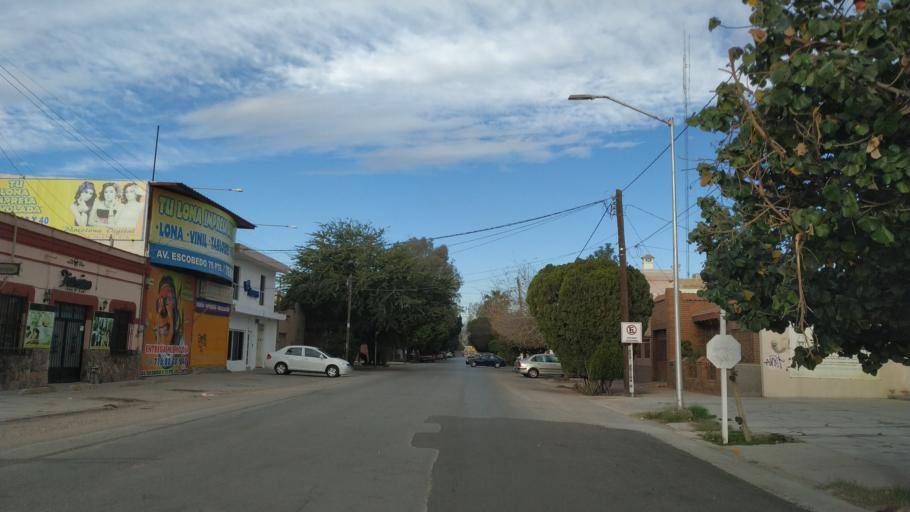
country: MX
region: Coahuila
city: Torreon
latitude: 25.5441
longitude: -103.4497
